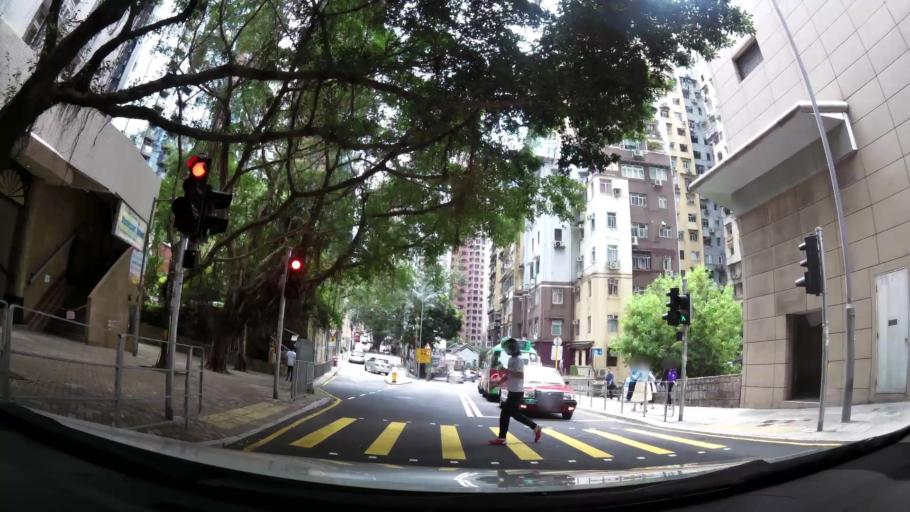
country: HK
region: Wanchai
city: Wan Chai
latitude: 22.2833
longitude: 114.1933
